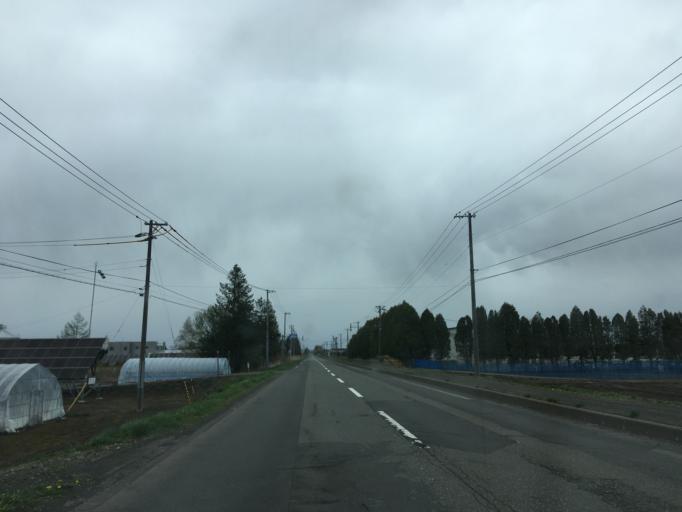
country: JP
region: Hokkaido
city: Chitose
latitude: 42.9307
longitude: 141.8069
